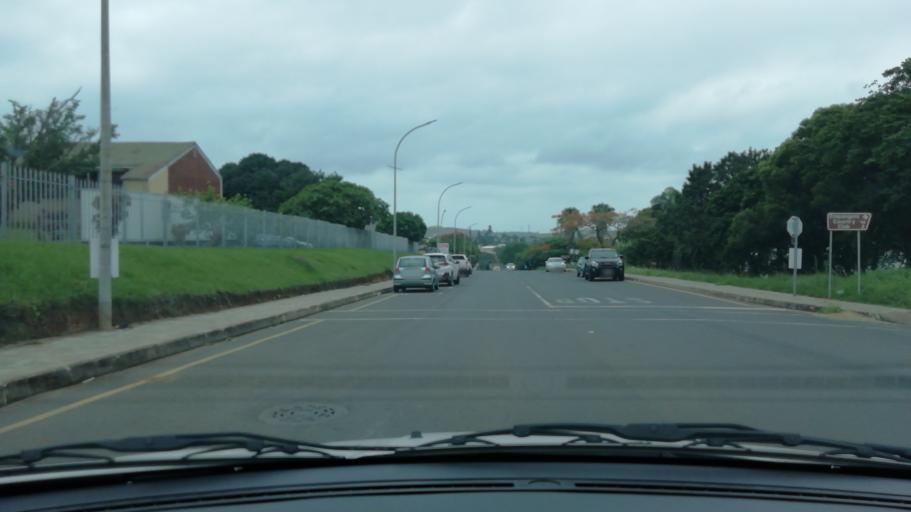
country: ZA
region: KwaZulu-Natal
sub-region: uThungulu District Municipality
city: Empangeni
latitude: -28.7440
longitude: 31.8925
